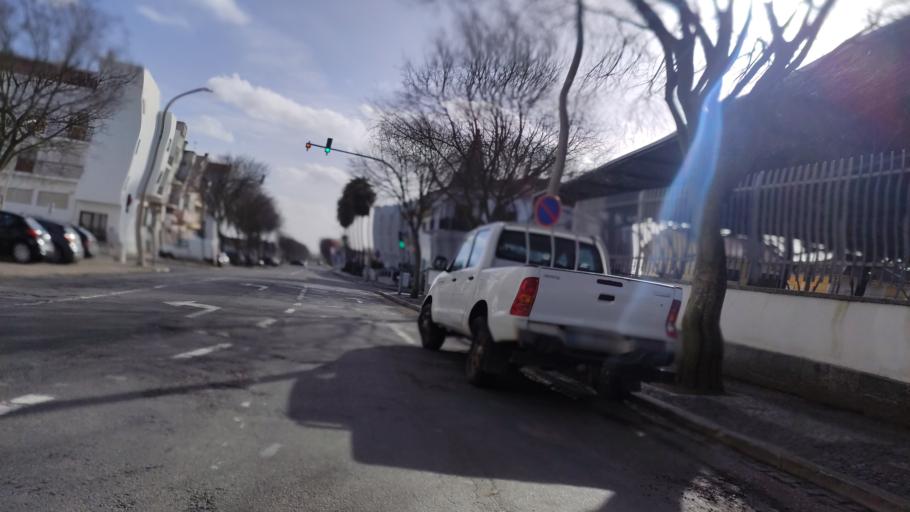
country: PT
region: Beja
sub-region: Beja
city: Beja
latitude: 38.0074
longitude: -7.8651
